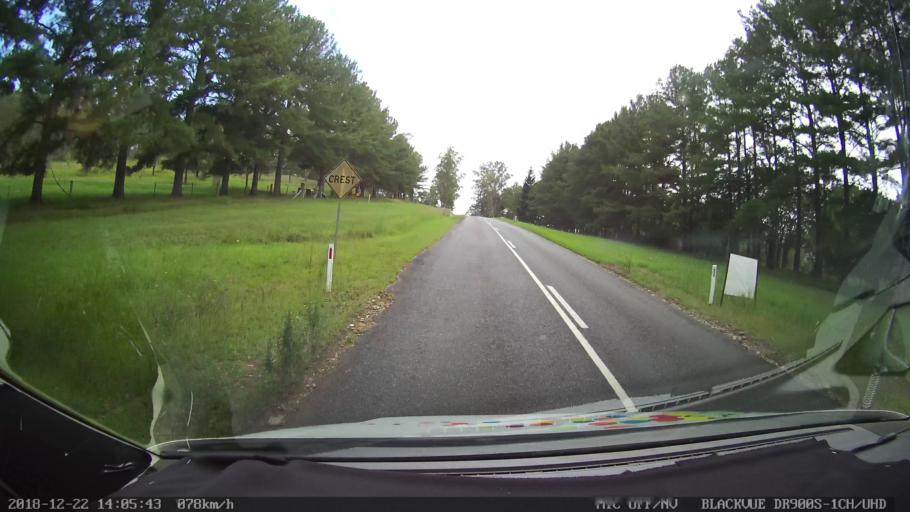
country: AU
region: New South Wales
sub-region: Clarence Valley
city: Coutts Crossing
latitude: -29.9480
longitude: 152.7290
